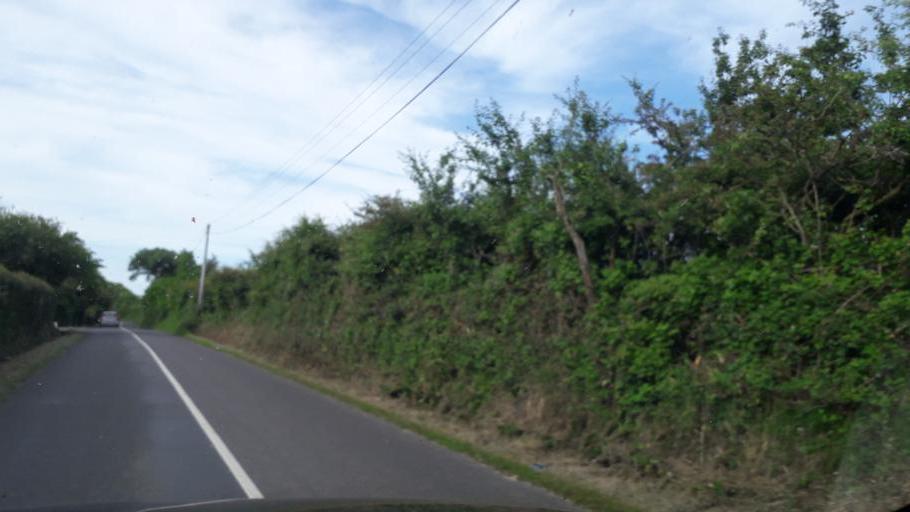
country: IE
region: Leinster
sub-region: Loch Garman
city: Courtown
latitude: 52.5596
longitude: -6.2338
